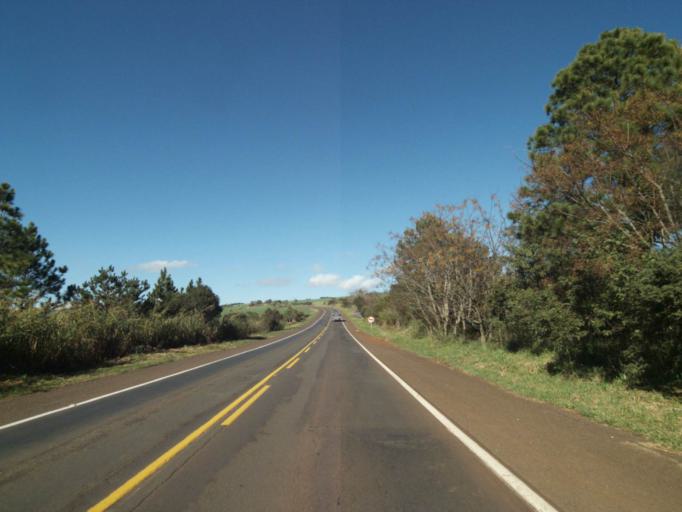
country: BR
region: Parana
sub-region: Faxinal
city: Faxinal
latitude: -23.8330
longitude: -51.1641
